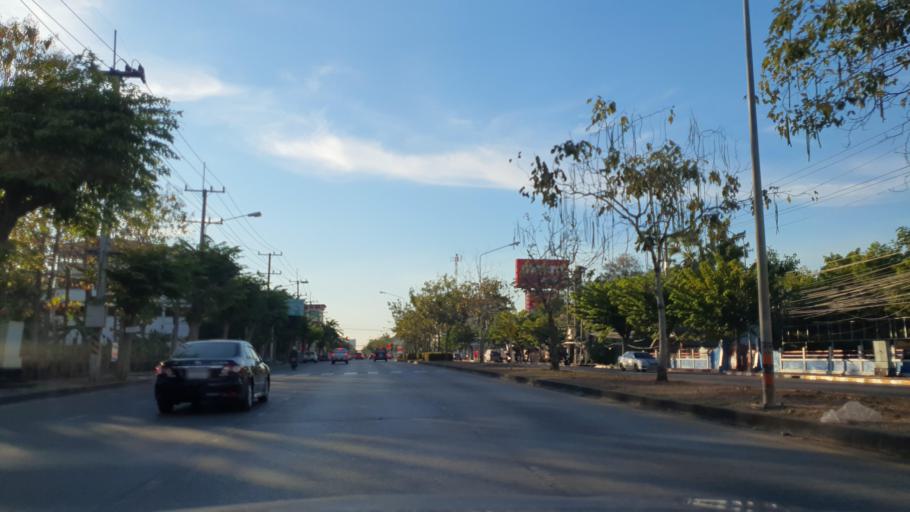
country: TH
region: Khon Kaen
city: Khon Kaen
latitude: 16.4270
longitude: 102.8729
